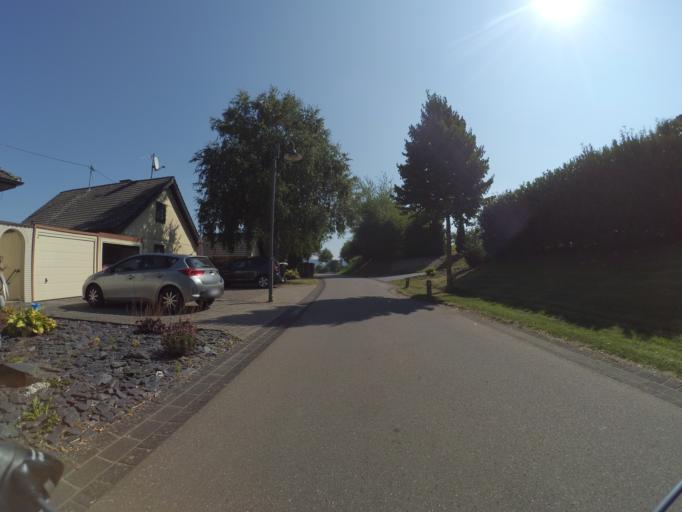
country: DE
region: Rheinland-Pfalz
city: Immert
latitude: 49.7643
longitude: 7.0226
